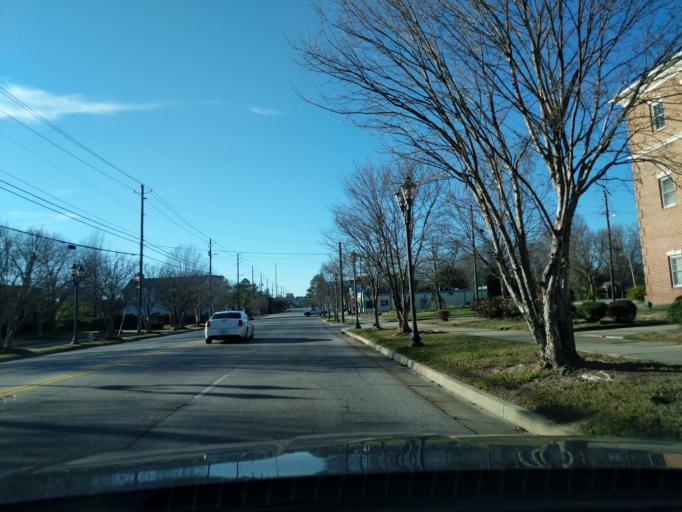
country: US
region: Georgia
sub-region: Richmond County
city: Augusta
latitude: 33.4641
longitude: -81.9748
